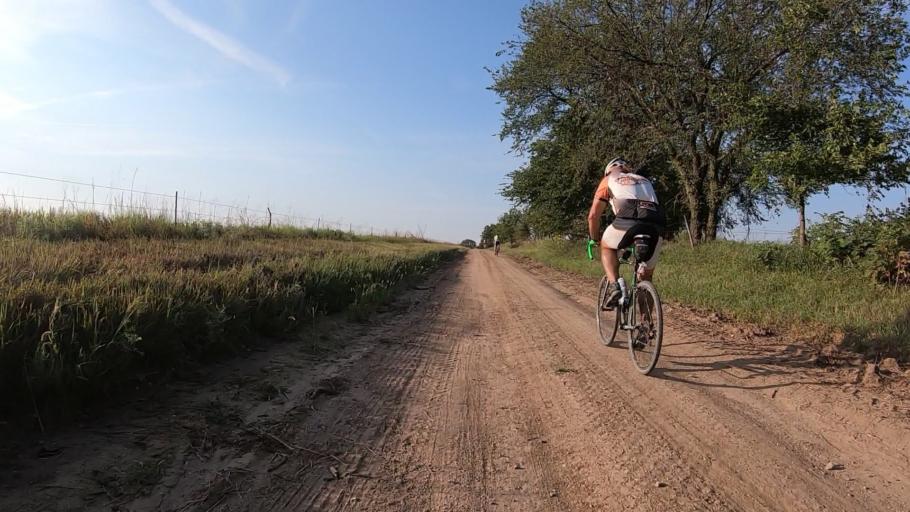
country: US
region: Kansas
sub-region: Marshall County
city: Blue Rapids
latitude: 39.7147
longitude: -96.8067
